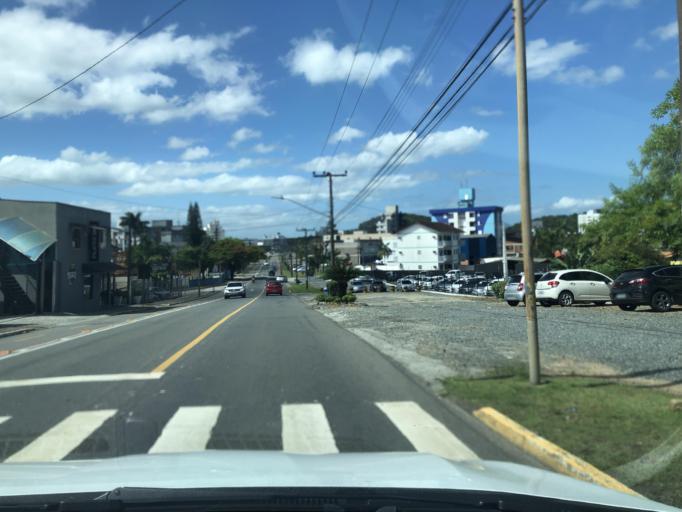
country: BR
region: Santa Catarina
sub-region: Joinville
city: Joinville
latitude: -26.2717
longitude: -48.8630
